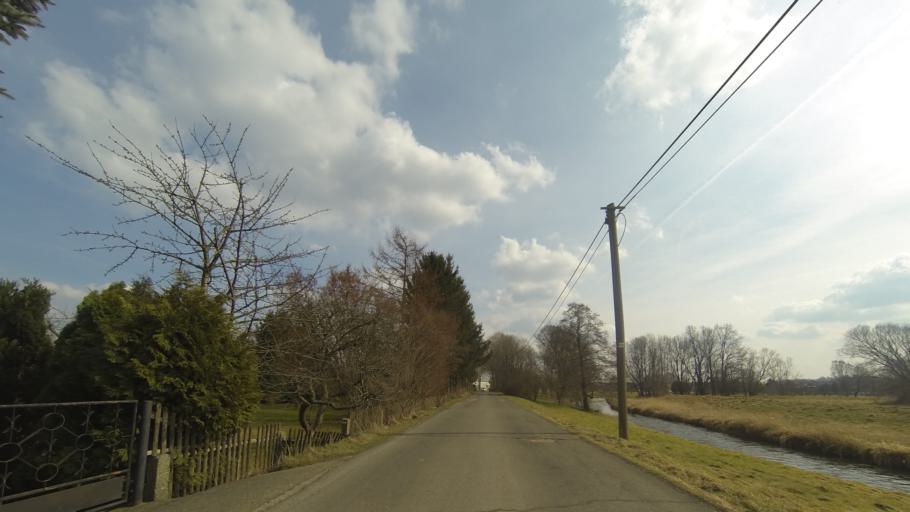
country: DE
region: Saxony
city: Radeburg
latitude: 51.2224
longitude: 13.7204
